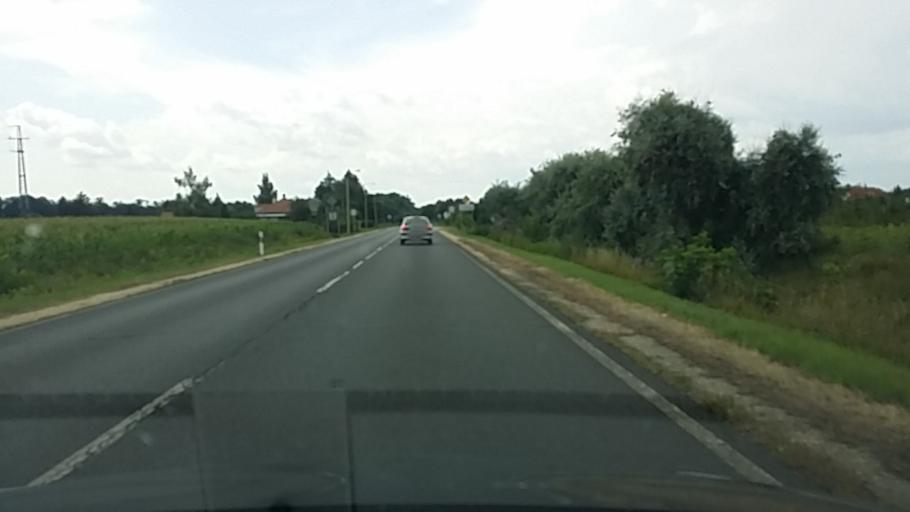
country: HU
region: Pest
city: Orkeny
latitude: 47.1205
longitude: 19.4398
